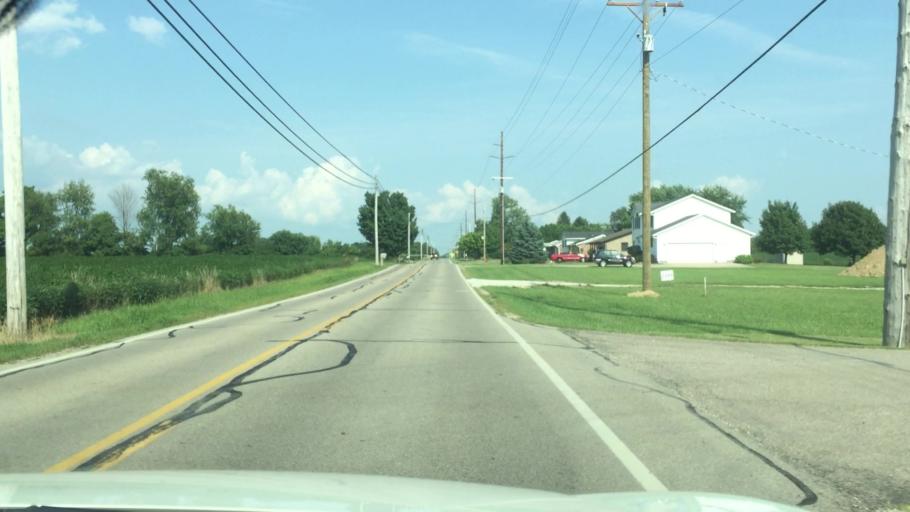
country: US
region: Ohio
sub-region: Clark County
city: Northridge
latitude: 39.9946
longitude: -83.7583
